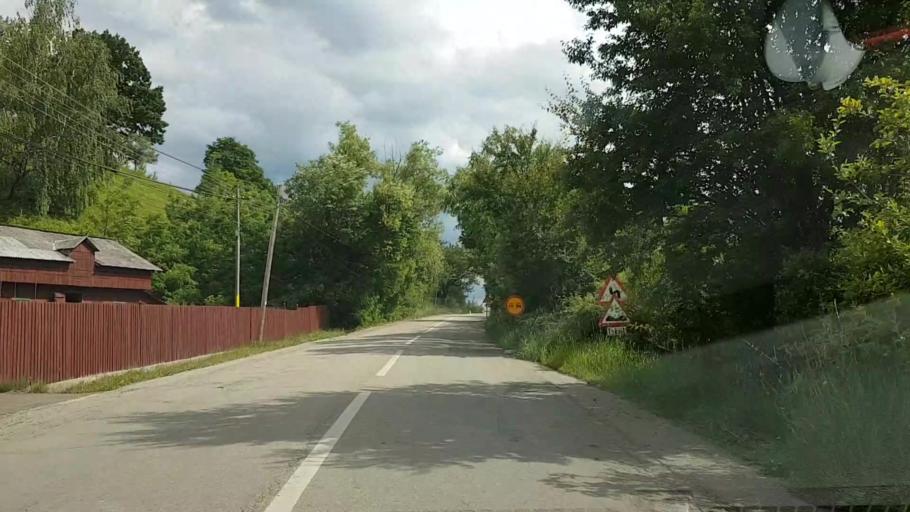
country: RO
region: Neamt
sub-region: Comuna Hangu
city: Hangu
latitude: 47.0410
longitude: 26.0567
